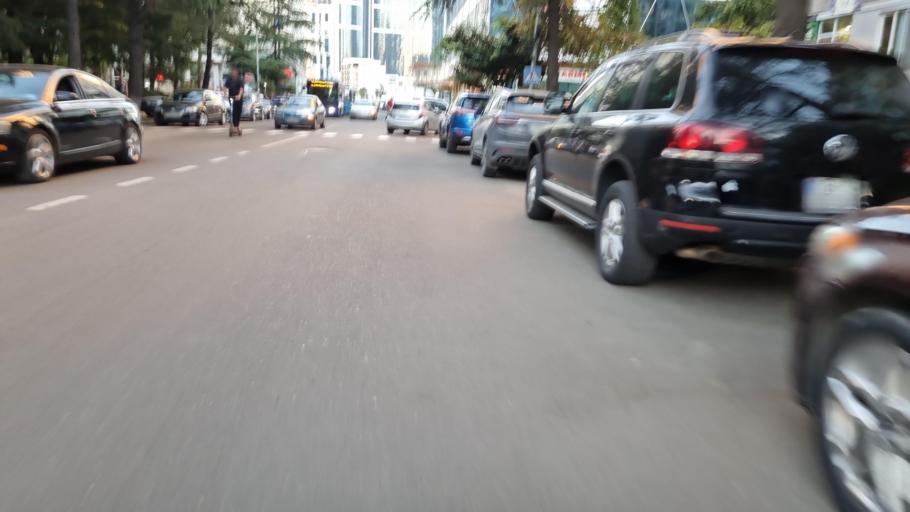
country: GE
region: Ajaria
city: Batumi
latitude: 41.6360
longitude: 41.6124
